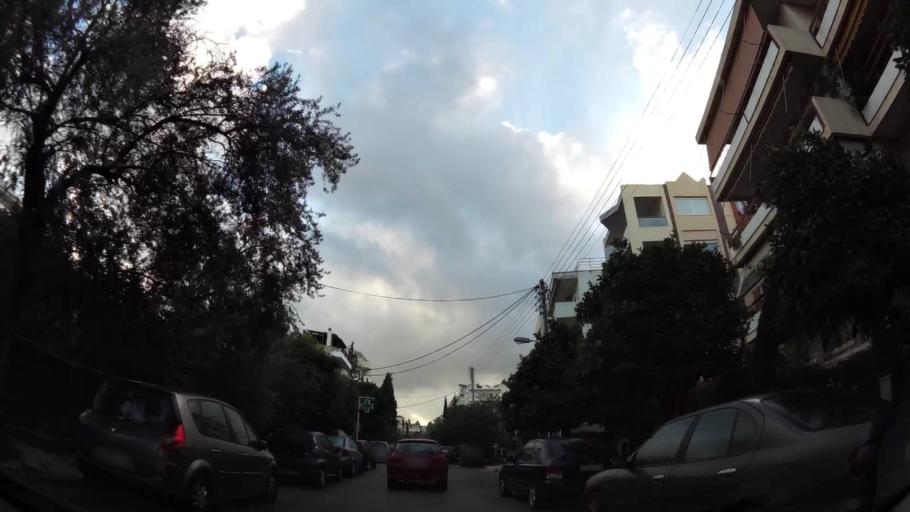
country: GR
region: Attica
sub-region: Nomarchia Athinas
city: Marousi
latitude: 38.0502
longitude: 23.8121
